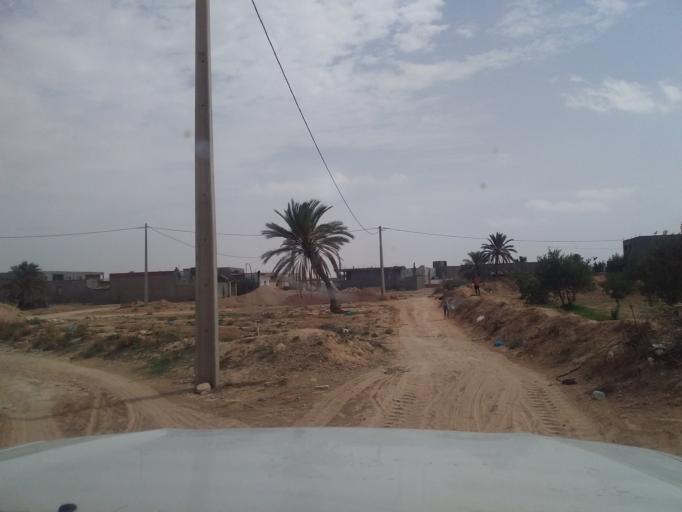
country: TN
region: Qabis
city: Matmata
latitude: 33.6147
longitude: 10.2764
